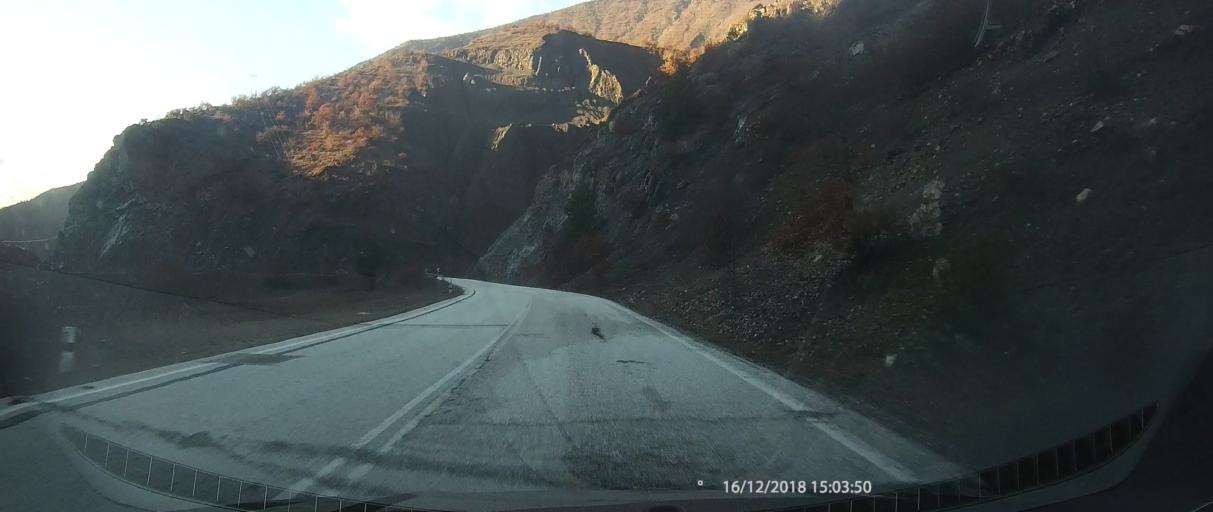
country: GR
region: West Macedonia
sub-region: Nomos Kastorias
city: Nestorio
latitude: 40.2282
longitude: 20.9768
